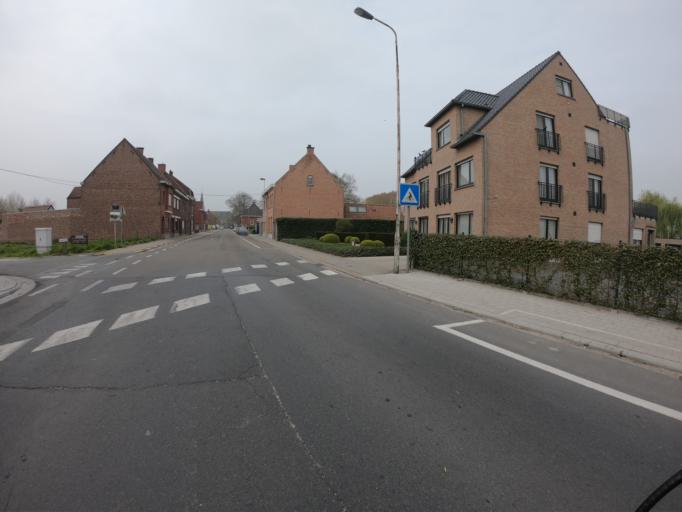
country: BE
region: Flanders
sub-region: Provincie West-Vlaanderen
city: Deerlijk
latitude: 50.8239
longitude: 3.3792
